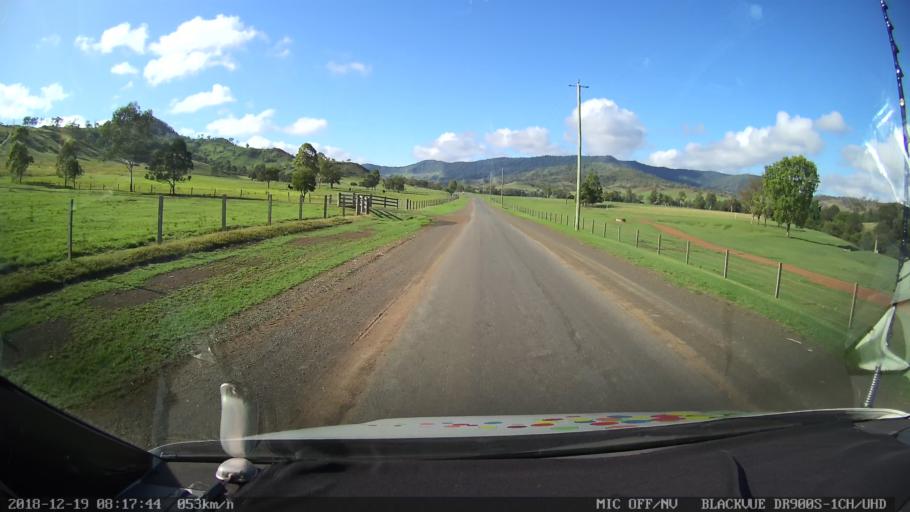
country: AU
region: New South Wales
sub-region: Kyogle
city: Kyogle
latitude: -28.2682
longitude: 152.9102
